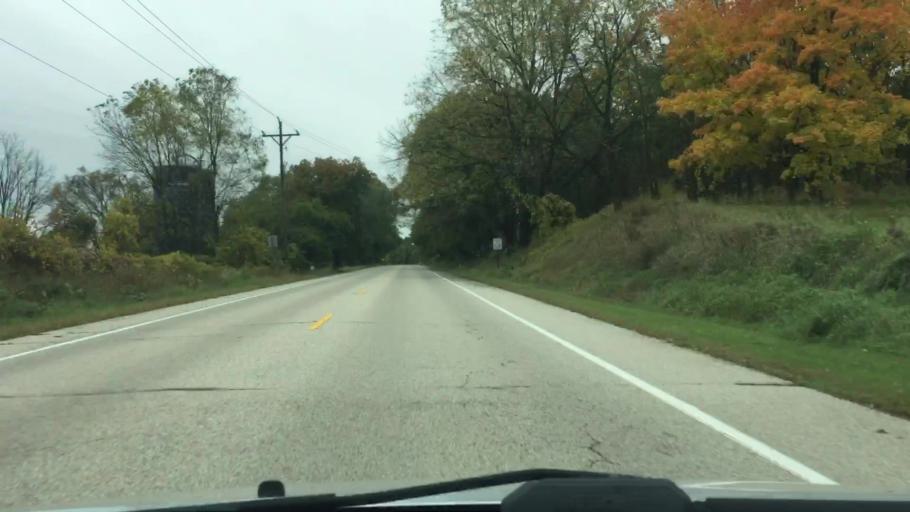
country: US
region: Wisconsin
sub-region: Waukesha County
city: Eagle
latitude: 42.8497
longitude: -88.5183
